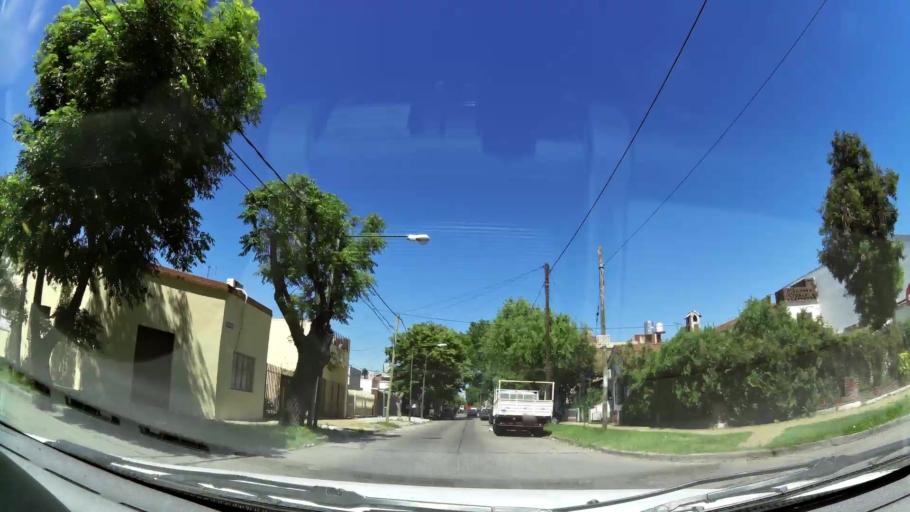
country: AR
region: Buenos Aires
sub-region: Partido de San Isidro
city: San Isidro
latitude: -34.5048
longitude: -58.5464
